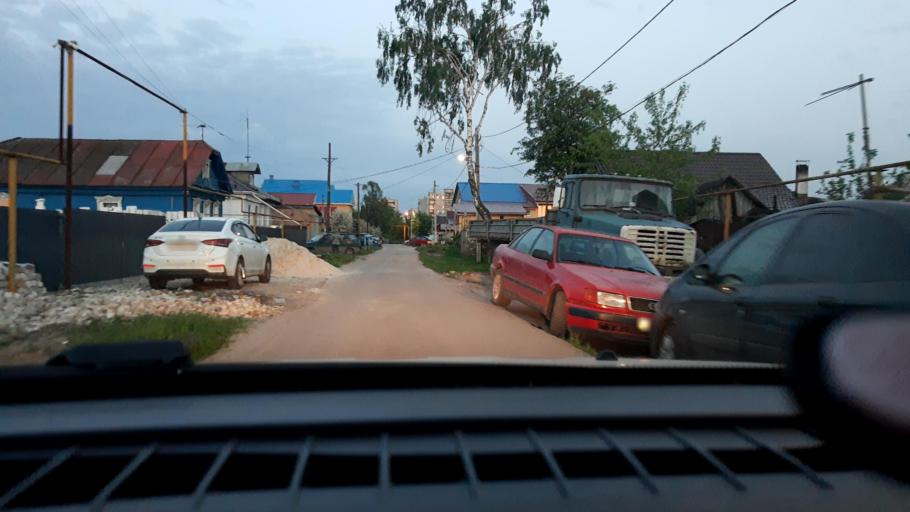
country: RU
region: Nizjnij Novgorod
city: Gorbatovka
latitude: 56.2759
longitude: 43.8750
